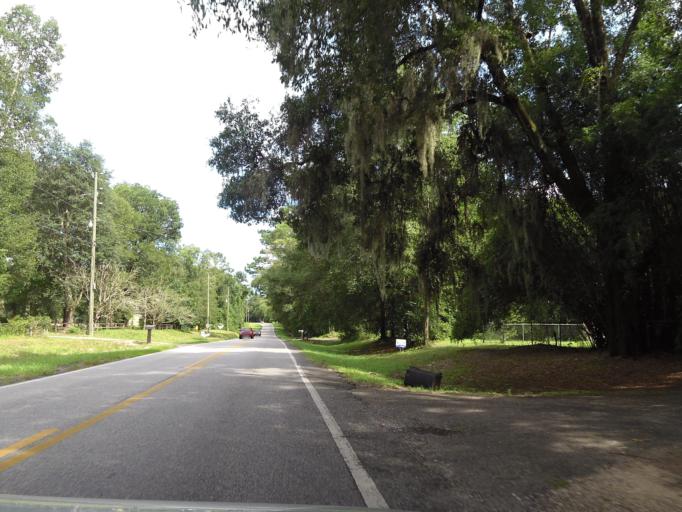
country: US
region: Florida
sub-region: Clay County
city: Green Cove Springs
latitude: 30.0379
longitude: -81.7310
